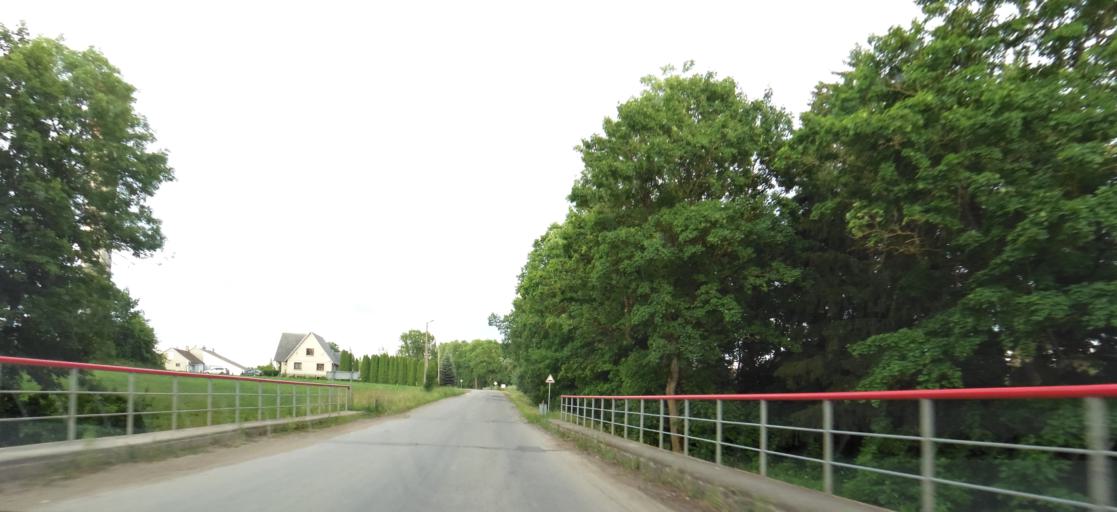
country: LT
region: Panevezys
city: Pasvalys
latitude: 56.0689
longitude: 24.4497
